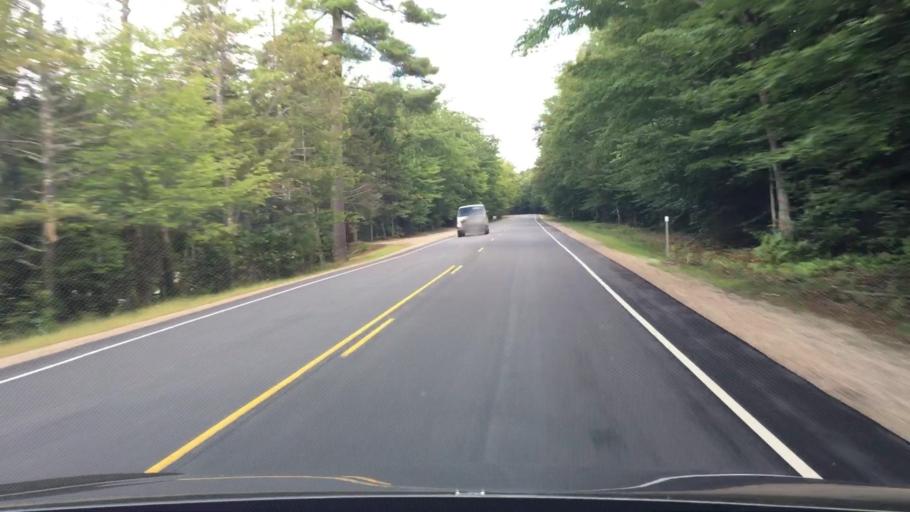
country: US
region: New Hampshire
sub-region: Carroll County
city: Conway
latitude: 43.9898
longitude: -71.1990
